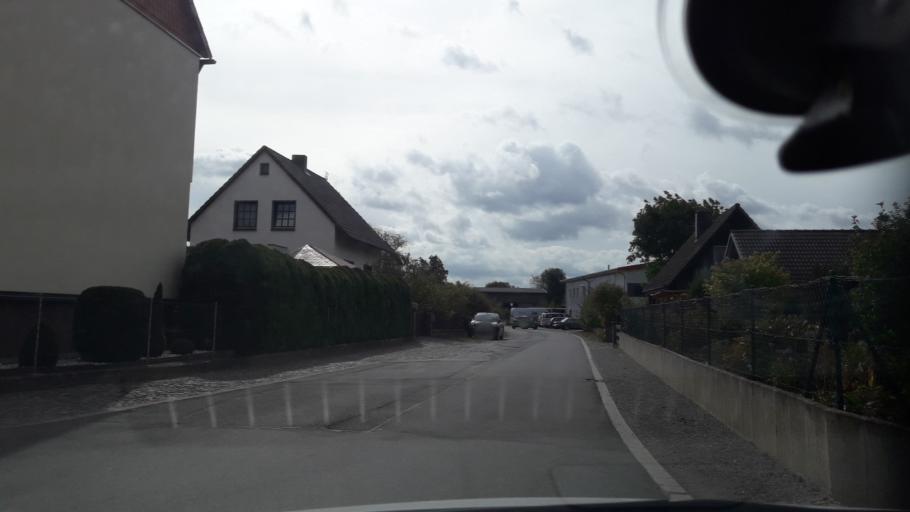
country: DE
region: Lower Saxony
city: Liebenburg
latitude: 52.0067
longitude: 10.3889
